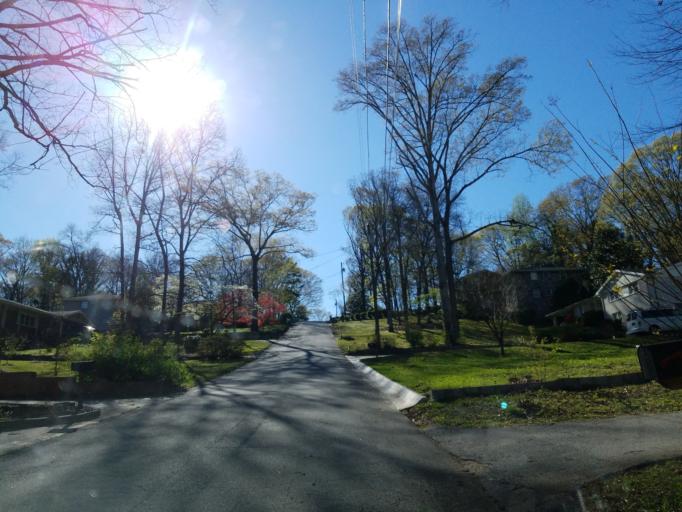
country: US
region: Georgia
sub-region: Cobb County
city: Marietta
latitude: 33.9736
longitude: -84.5163
